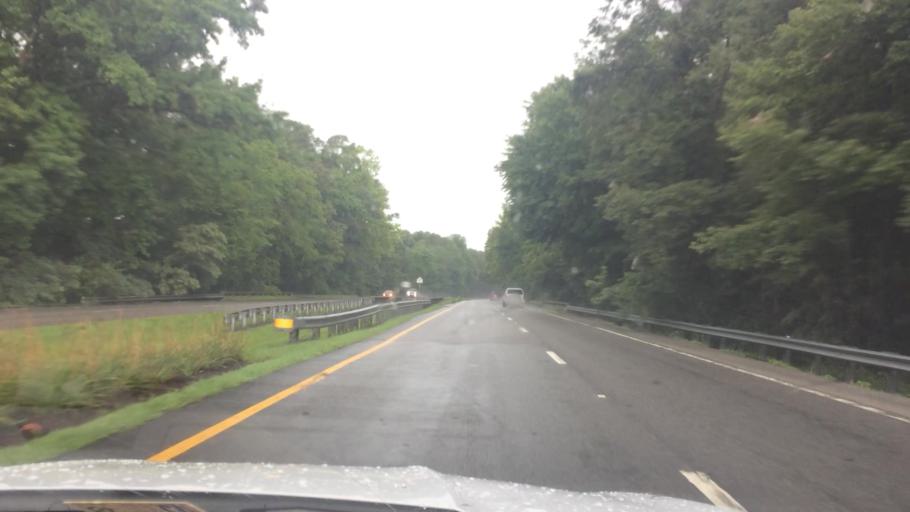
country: US
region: Virginia
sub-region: York County
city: Yorktown
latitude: 37.2041
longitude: -76.5038
